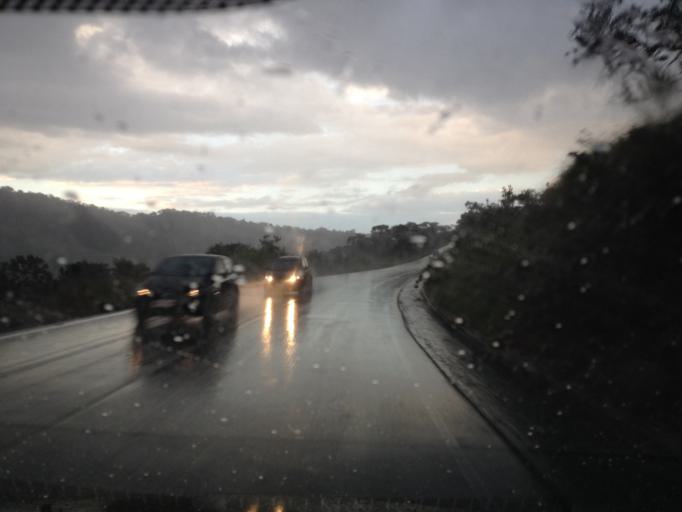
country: BR
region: Minas Gerais
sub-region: Caxambu
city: Caxambu
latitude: -21.9884
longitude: -44.9913
